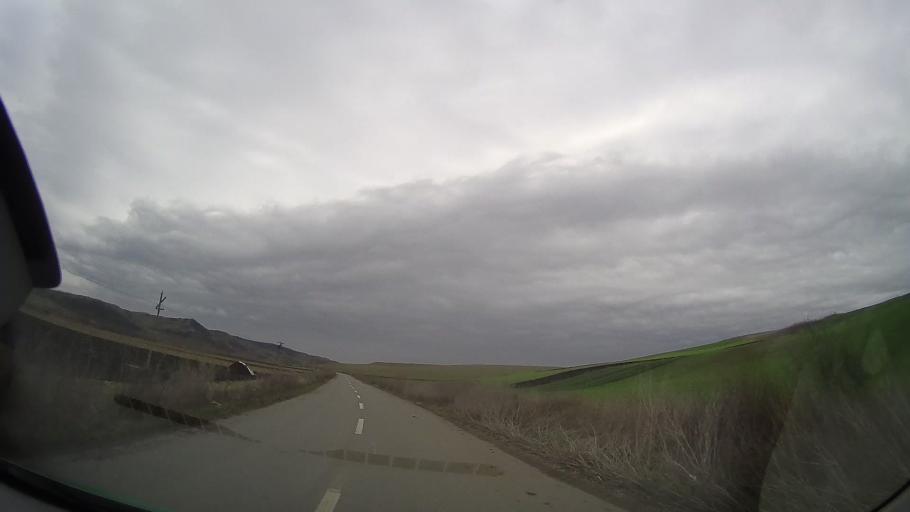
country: RO
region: Bistrita-Nasaud
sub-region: Comuna Milas
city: Milas
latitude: 46.7908
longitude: 24.4216
